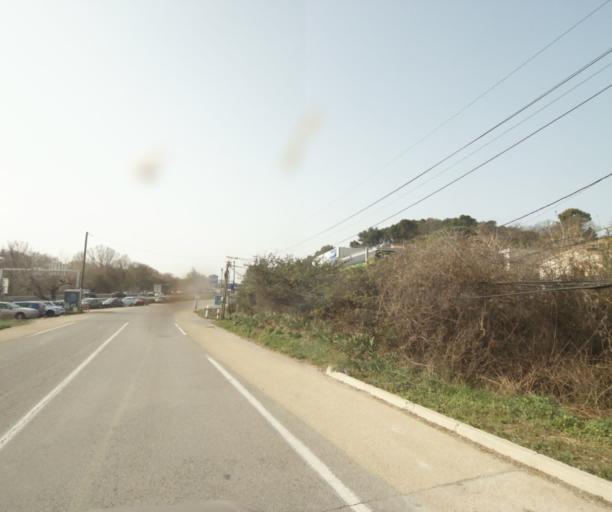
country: FR
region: Provence-Alpes-Cote d'Azur
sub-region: Departement des Bouches-du-Rhone
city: Aix-en-Provence
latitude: 43.5122
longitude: 5.4221
